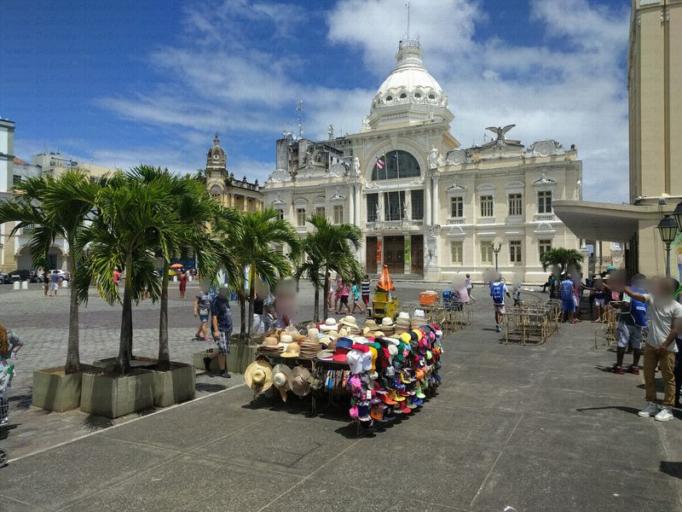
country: BR
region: Bahia
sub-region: Salvador
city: Salvador
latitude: -12.9743
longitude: -38.5127
